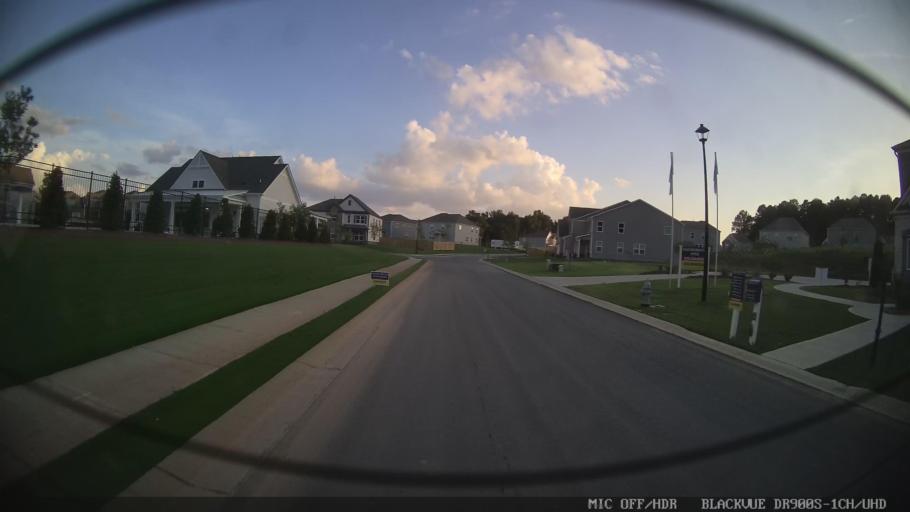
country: US
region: Georgia
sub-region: Forsyth County
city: Cumming
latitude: 34.2206
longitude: -84.2084
